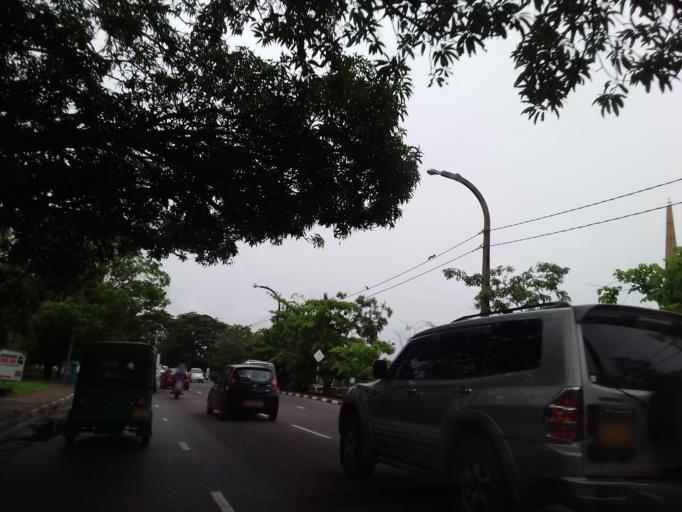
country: LK
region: Western
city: Battaramulla South
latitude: 6.8939
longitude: 79.9165
